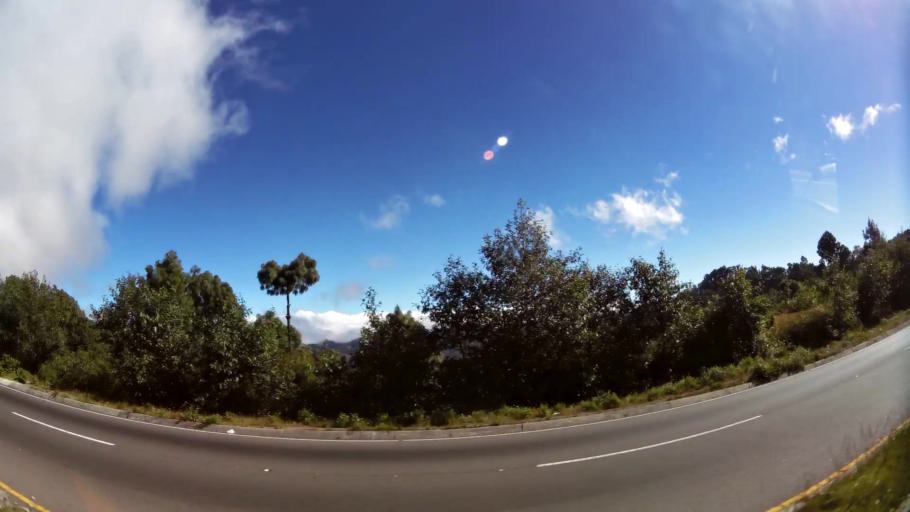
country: GT
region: Solola
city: Santa Catarina Ixtahuacan
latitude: 14.8289
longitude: -91.3621
